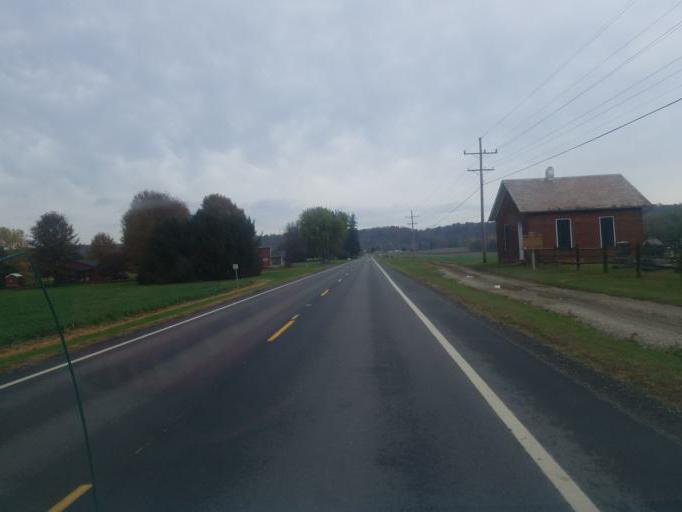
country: US
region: Ohio
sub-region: Washington County
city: Beverly
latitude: 39.5548
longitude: -81.5866
